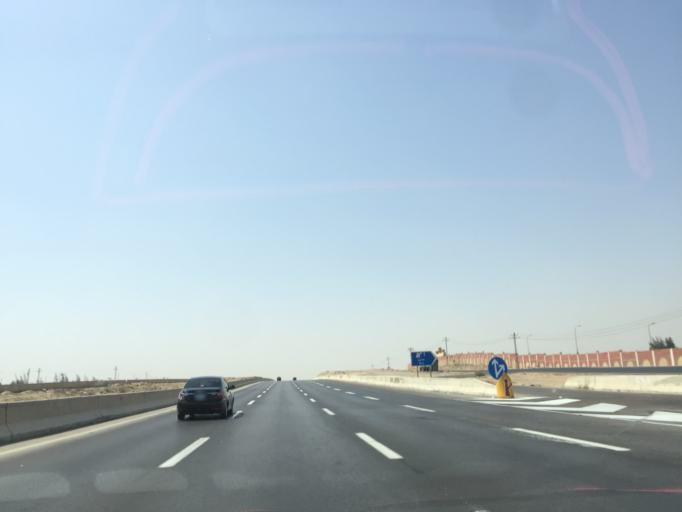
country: EG
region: Al Jizah
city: Awsim
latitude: 30.0856
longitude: 30.9844
